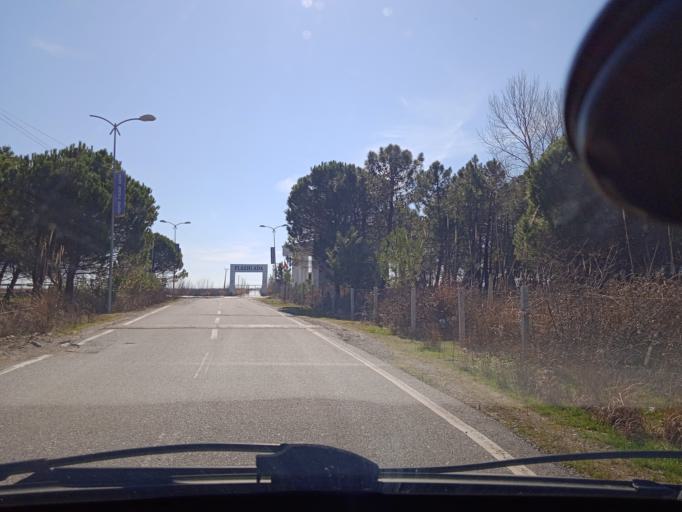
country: AL
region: Shkoder
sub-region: Rrethi i Shkodres
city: Velipoje
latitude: 41.8634
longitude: 19.4065
